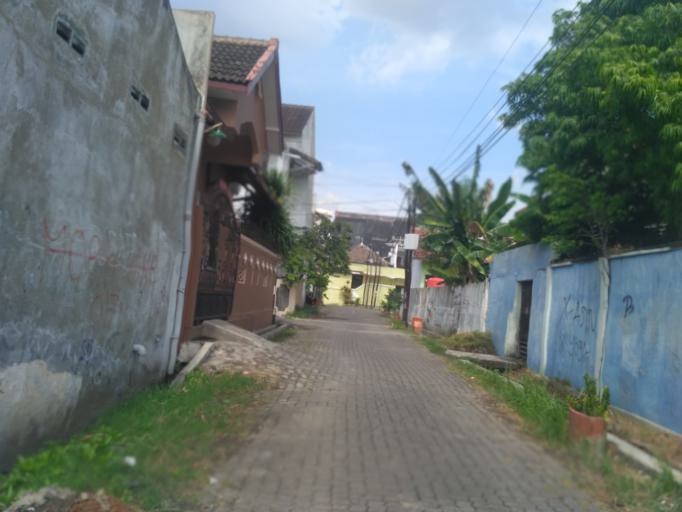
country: ID
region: Central Java
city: Semarang
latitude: -6.9586
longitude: 110.4019
